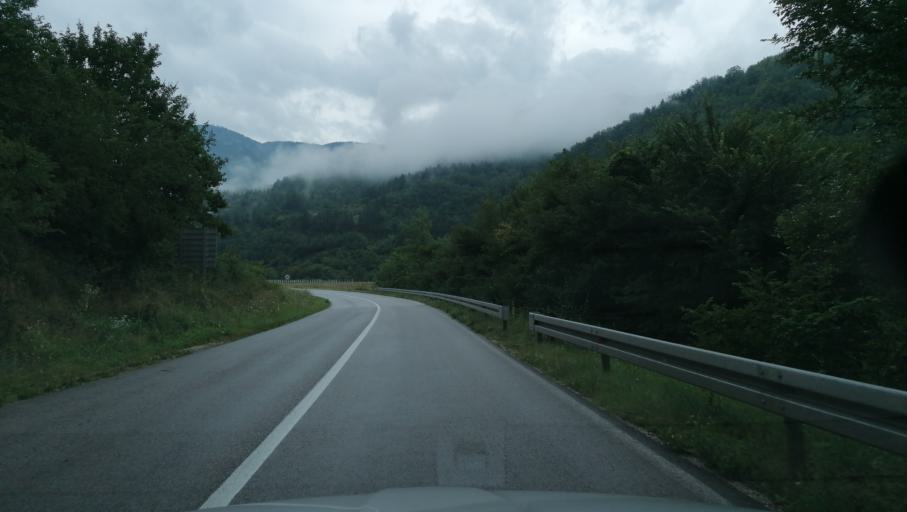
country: RS
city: Durici
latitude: 43.7628
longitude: 19.3868
